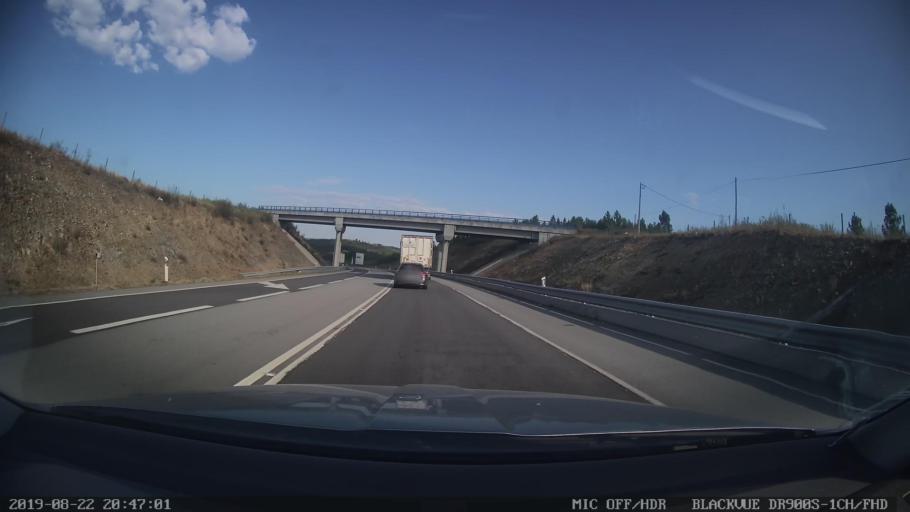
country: PT
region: Castelo Branco
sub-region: Proenca-A-Nova
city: Proenca-a-Nova
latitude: 39.7317
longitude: -7.8824
